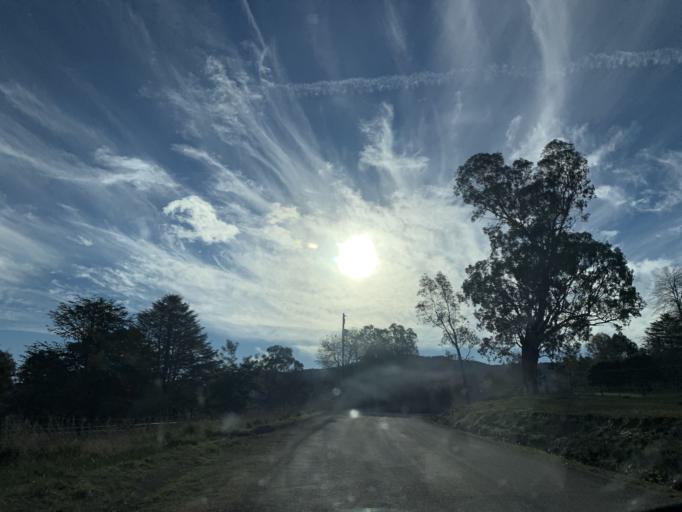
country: AU
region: Victoria
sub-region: Mansfield
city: Mansfield
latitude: -36.9553
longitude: 146.1000
